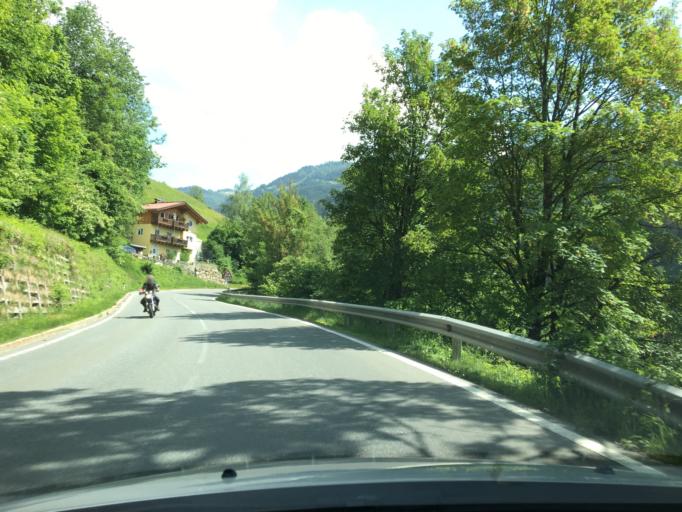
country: AT
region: Salzburg
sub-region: Politischer Bezirk Sankt Johann im Pongau
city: Sankt Johann im Pongau
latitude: 47.3400
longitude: 13.2123
